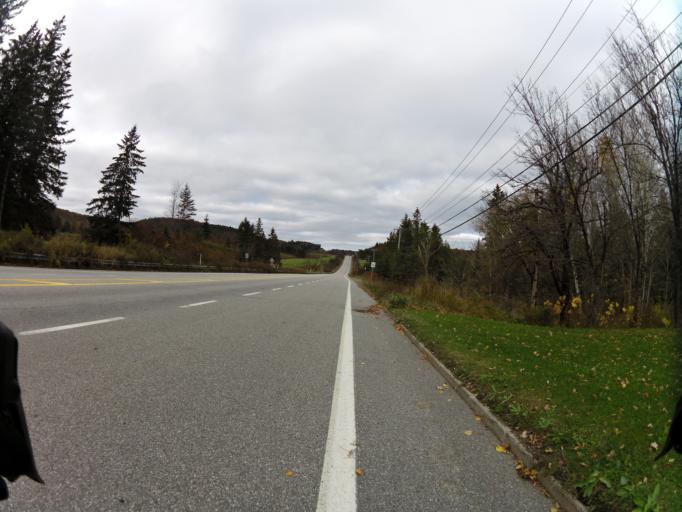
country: CA
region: Quebec
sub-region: Outaouais
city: Wakefield
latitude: 45.6000
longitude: -75.9010
